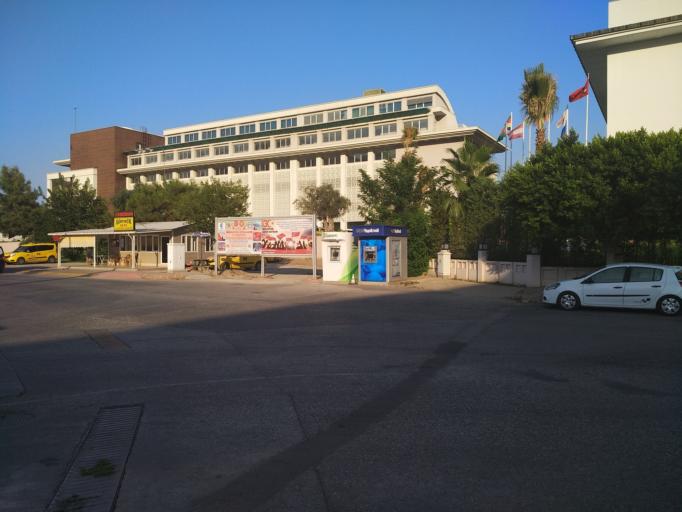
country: TR
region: Antalya
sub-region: Kemer
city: Goeynuek
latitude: 36.6640
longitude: 30.5602
